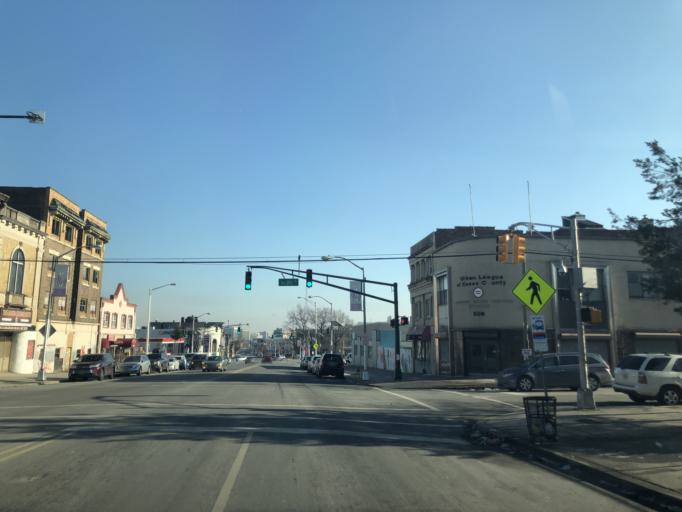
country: US
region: New Jersey
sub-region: Essex County
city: East Orange
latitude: 40.7486
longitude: -74.1950
